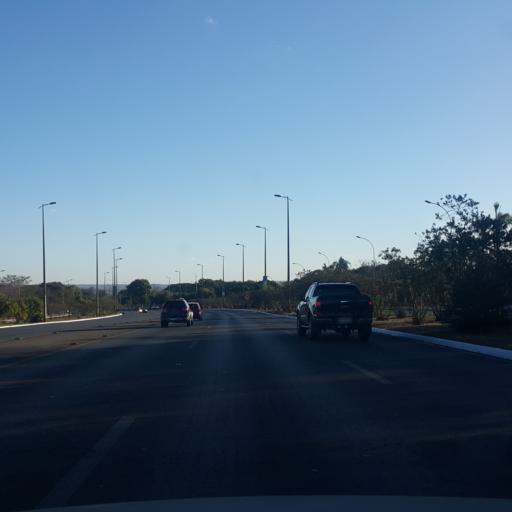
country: BR
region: Federal District
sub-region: Brasilia
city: Brasilia
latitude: -15.8366
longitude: -47.9280
